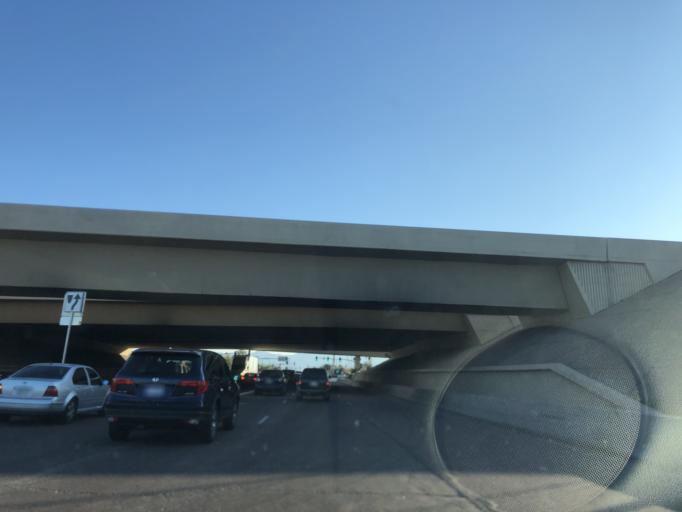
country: US
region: Arizona
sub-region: Maricopa County
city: Tolleson
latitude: 33.4623
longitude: -112.2727
